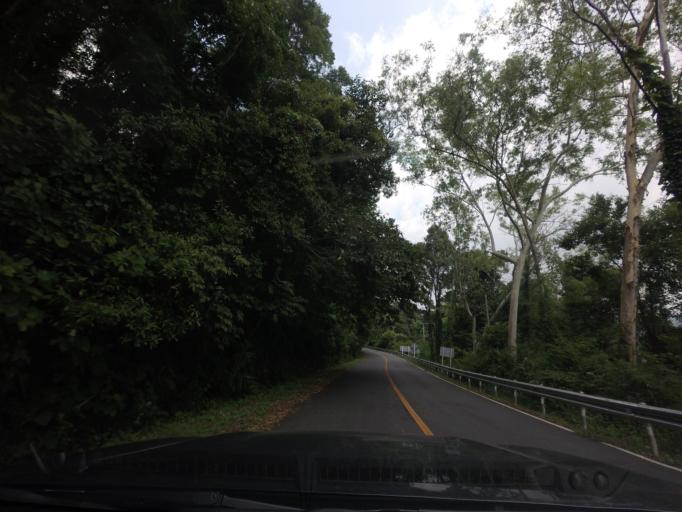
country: TH
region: Nan
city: Pua
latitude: 19.1827
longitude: 100.9924
